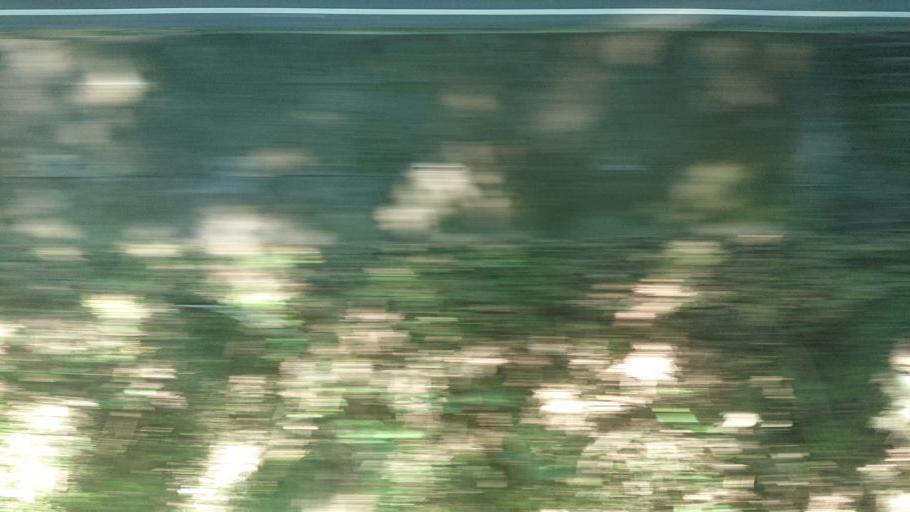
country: TW
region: Taiwan
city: Lugu
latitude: 23.4879
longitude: 120.7604
